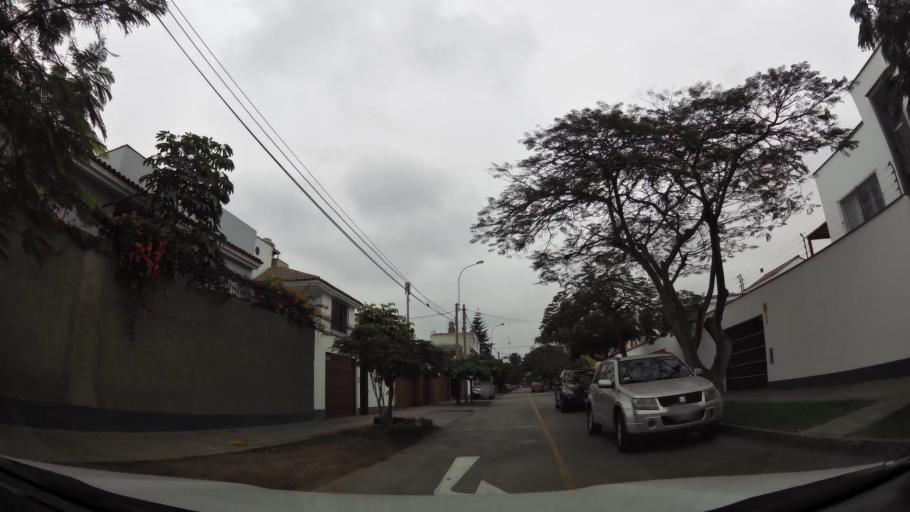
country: PE
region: Lima
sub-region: Lima
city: San Luis
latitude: -12.1051
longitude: -77.0057
